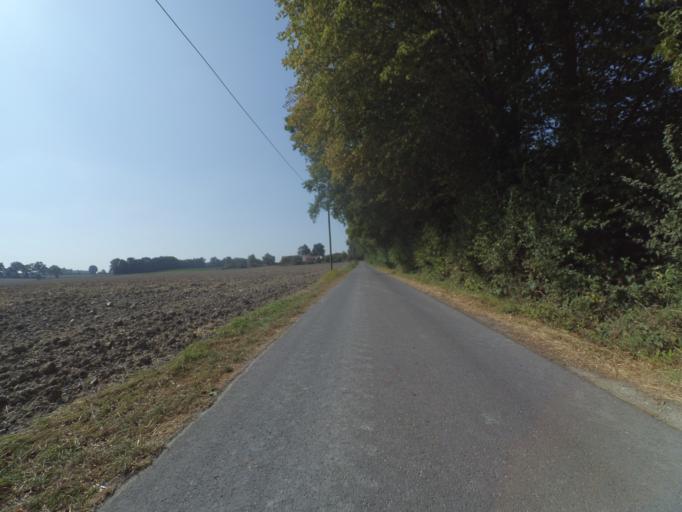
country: DE
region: North Rhine-Westphalia
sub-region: Regierungsbezirk Munster
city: Schoppingen
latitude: 52.0759
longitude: 7.1814
